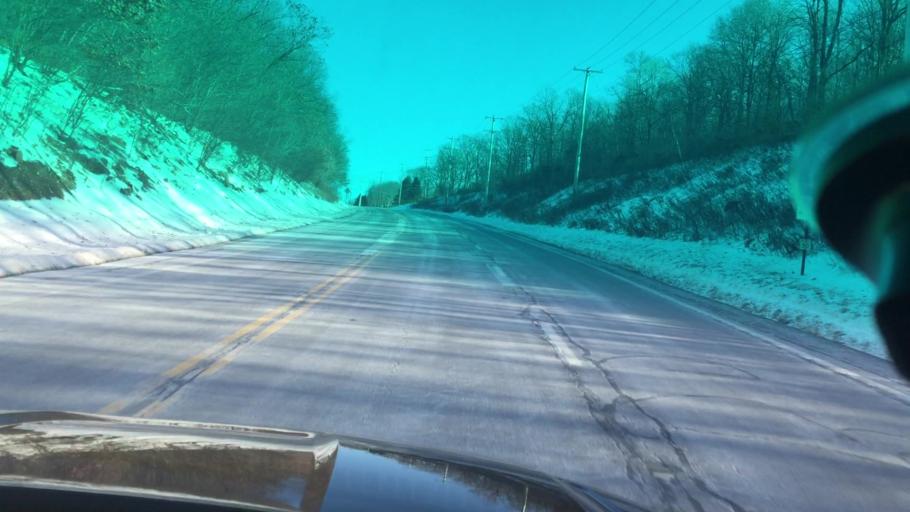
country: US
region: Pennsylvania
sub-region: Luzerne County
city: Oakdale
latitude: 41.0179
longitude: -75.9277
